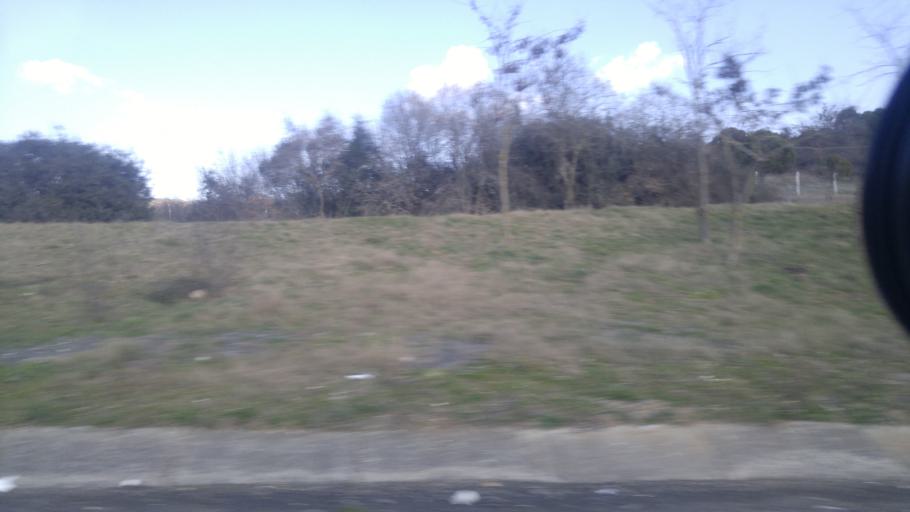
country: TR
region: Istanbul
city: Canta
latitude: 41.1669
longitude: 28.1257
